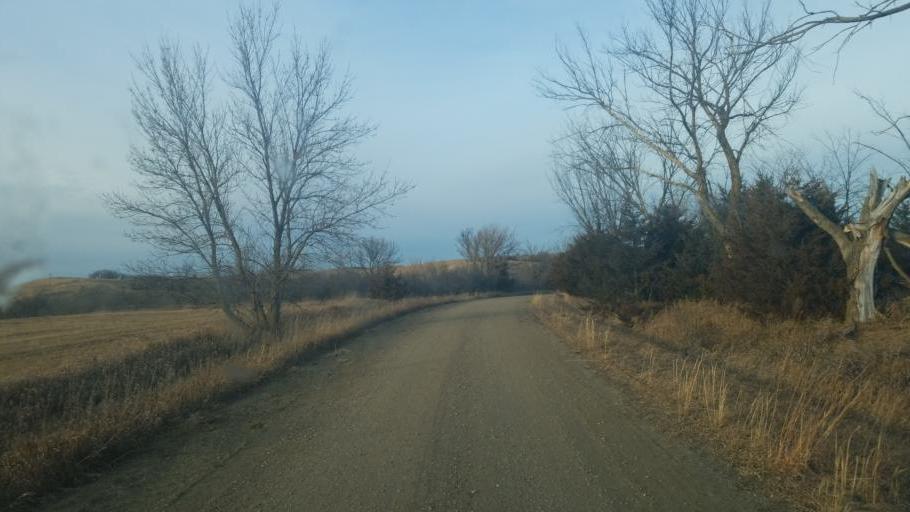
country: US
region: Nebraska
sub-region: Knox County
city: Center
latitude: 42.6829
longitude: -97.8185
